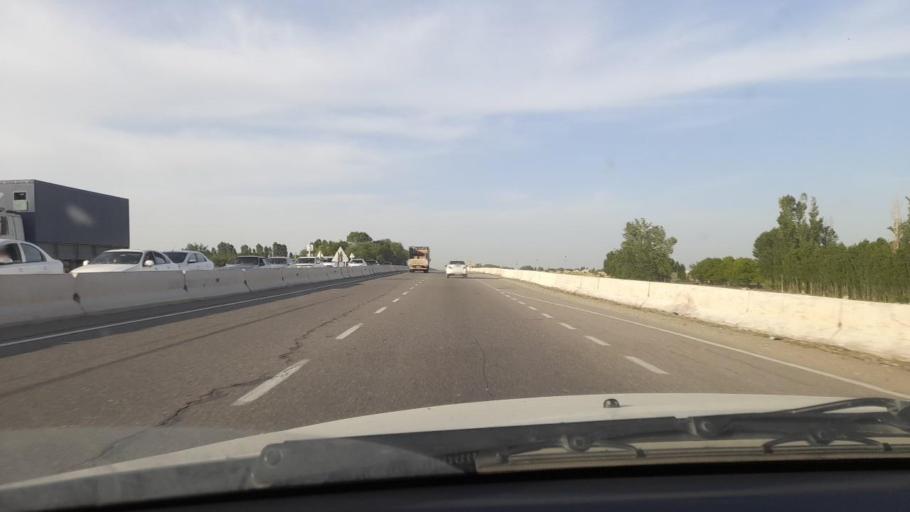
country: UZ
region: Jizzax
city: Paxtakor
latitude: 40.3156
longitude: 68.0900
